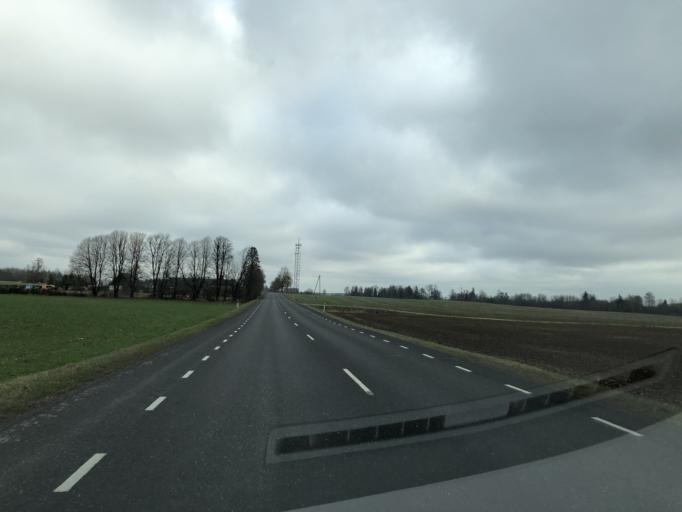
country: EE
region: Laeaene-Virumaa
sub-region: Rakvere linn
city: Rakvere
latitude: 59.2828
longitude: 26.2975
